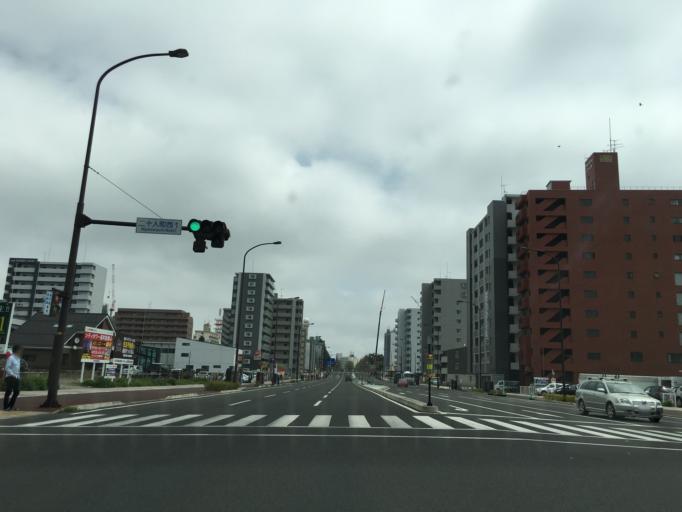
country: JP
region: Miyagi
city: Sendai-shi
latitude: 38.2626
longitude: 140.8895
